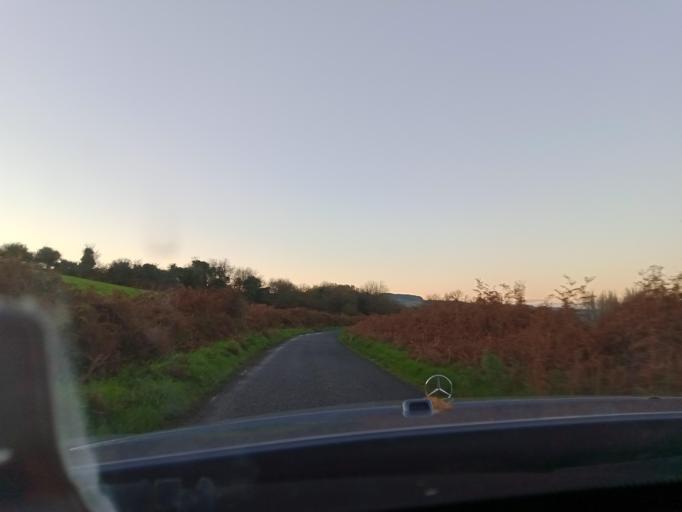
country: IE
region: Leinster
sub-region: Kilkenny
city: Thomastown
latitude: 52.4324
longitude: -7.1039
